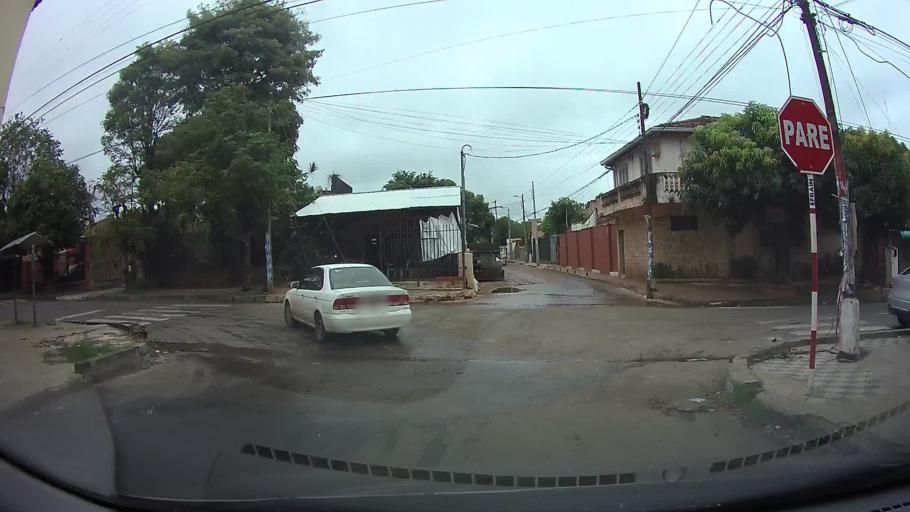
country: PY
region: Central
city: Lambare
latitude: -25.3333
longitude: -57.5830
